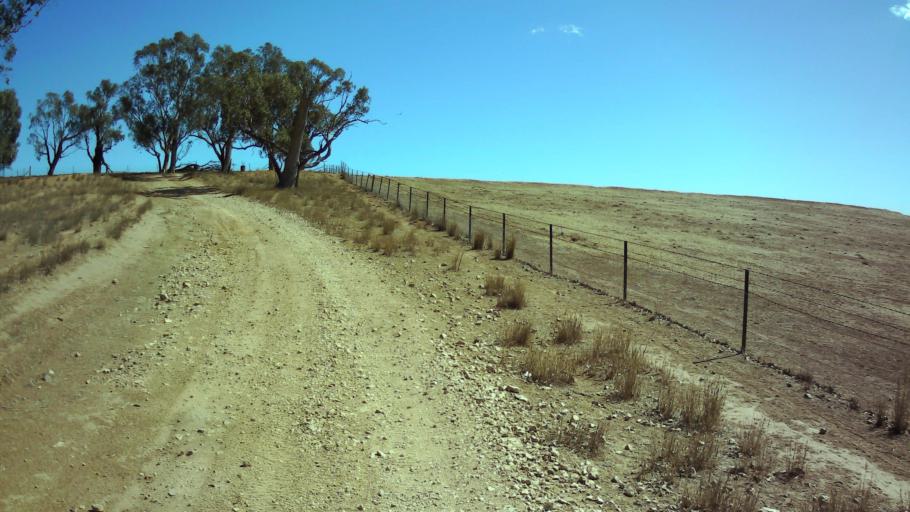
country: AU
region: New South Wales
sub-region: Weddin
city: Grenfell
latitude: -33.9971
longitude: 148.4372
